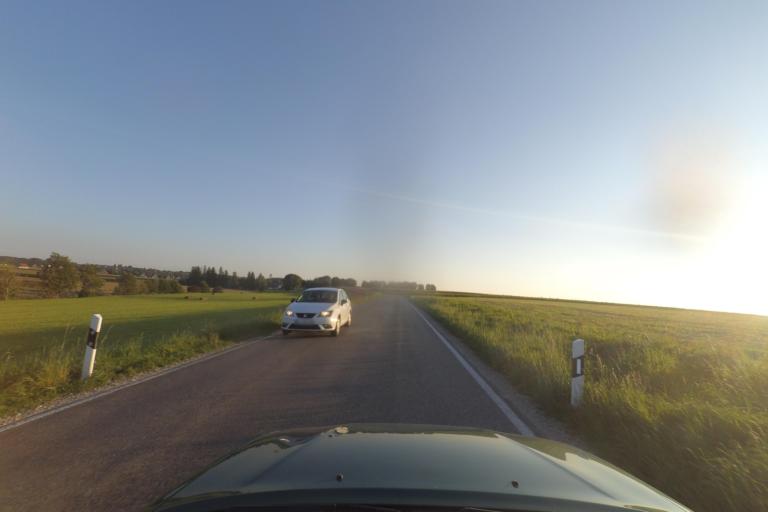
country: DE
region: Bavaria
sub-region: Upper Bavaria
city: Weil
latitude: 48.1078
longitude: 10.9088
